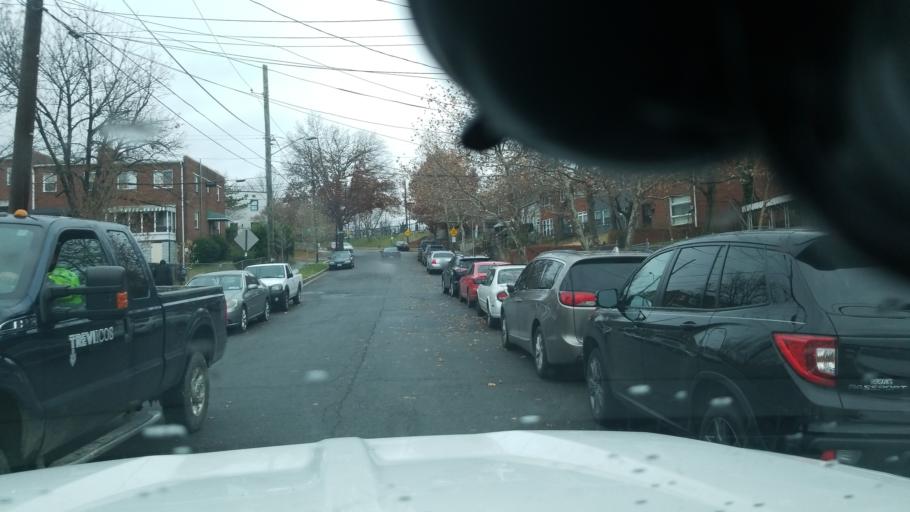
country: US
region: Maryland
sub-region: Prince George's County
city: Mount Rainier
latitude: 38.9193
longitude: -76.9832
